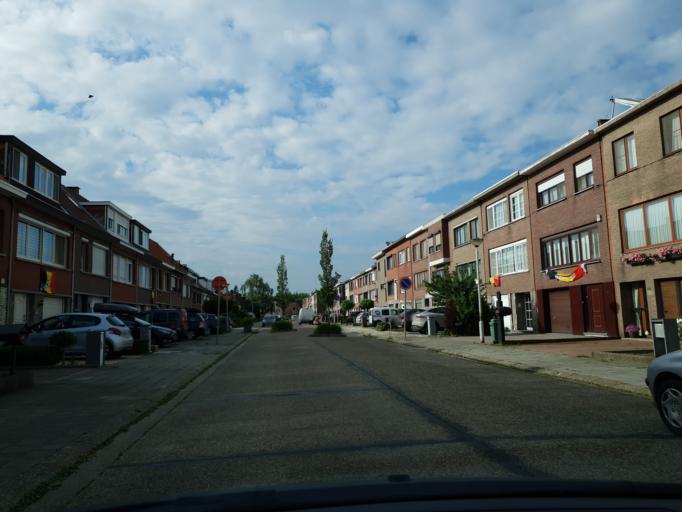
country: BE
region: Flanders
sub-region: Provincie Antwerpen
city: Kapellen
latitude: 51.2780
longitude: 4.4380
